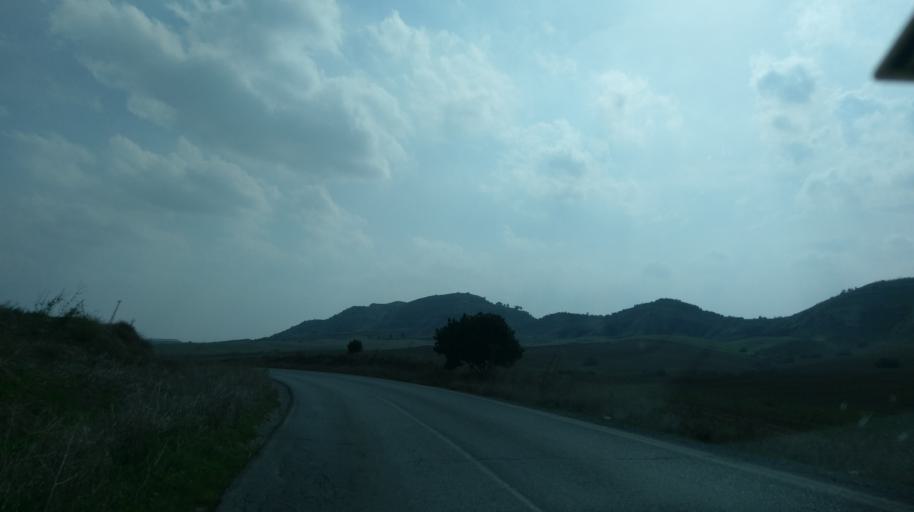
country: CY
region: Keryneia
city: Lapithos
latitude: 35.2596
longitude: 33.1310
